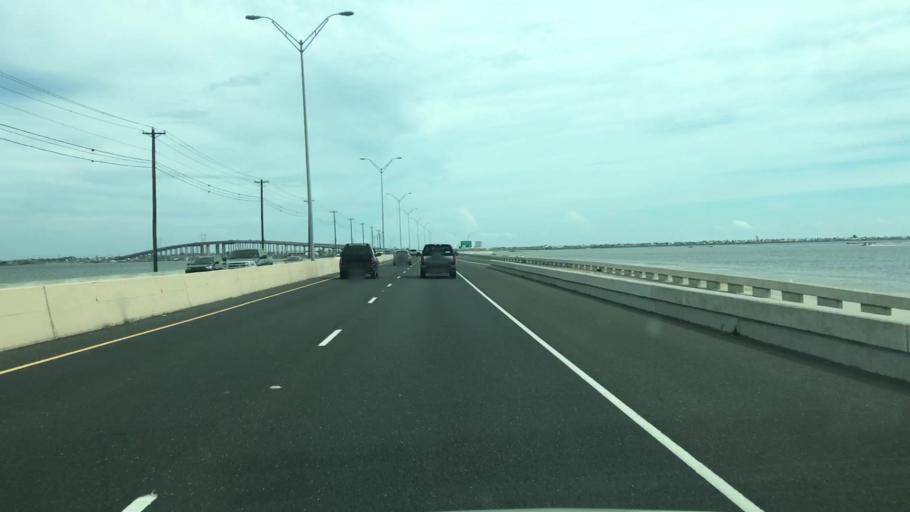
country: US
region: Texas
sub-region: Nueces County
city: Corpus Christi
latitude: 27.6433
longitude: -97.2491
